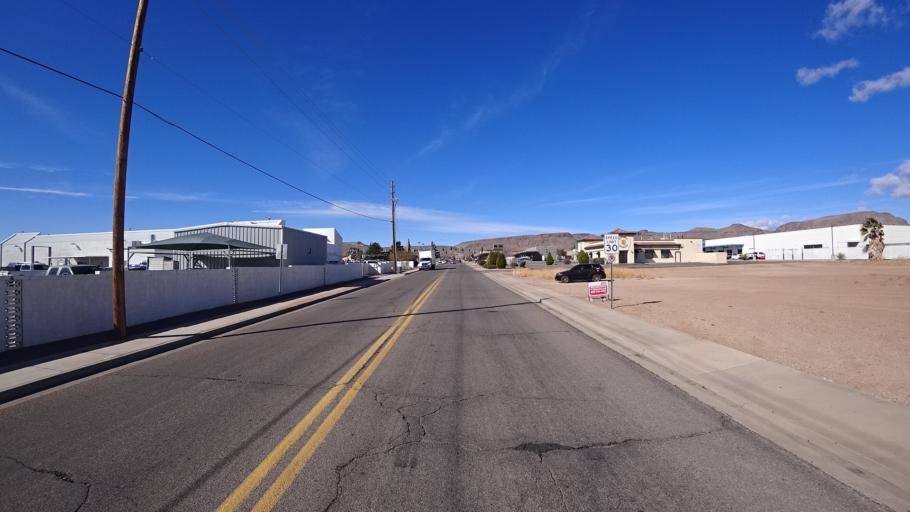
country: US
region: Arizona
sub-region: Mohave County
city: New Kingman-Butler
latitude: 35.2322
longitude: -114.0350
